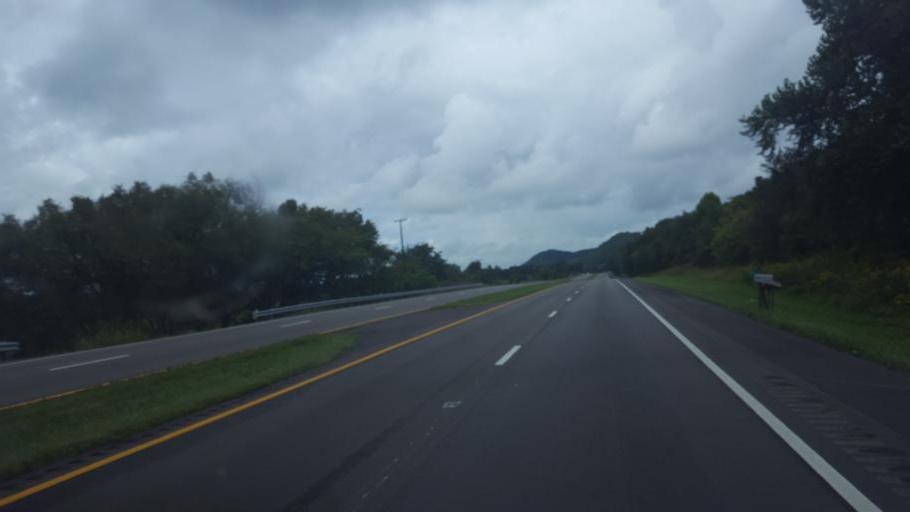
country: US
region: Ohio
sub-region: Scioto County
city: Rosemount
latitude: 38.8126
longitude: -82.9850
